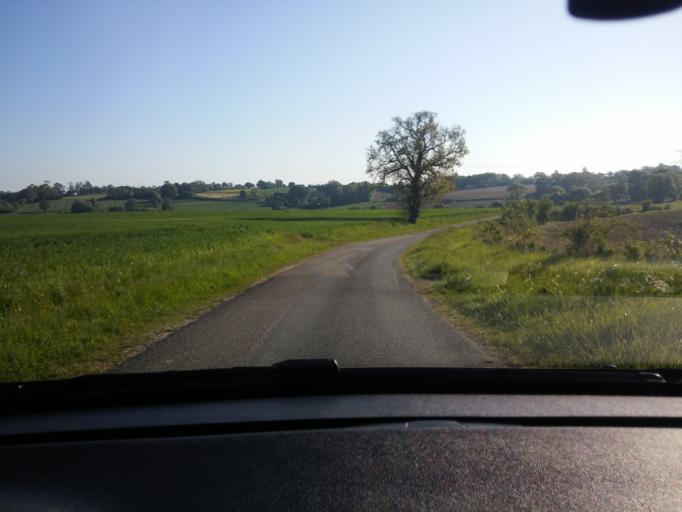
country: FR
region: Aquitaine
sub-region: Departement du Lot-et-Garonne
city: Laplume
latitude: 44.0899
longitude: 0.5245
